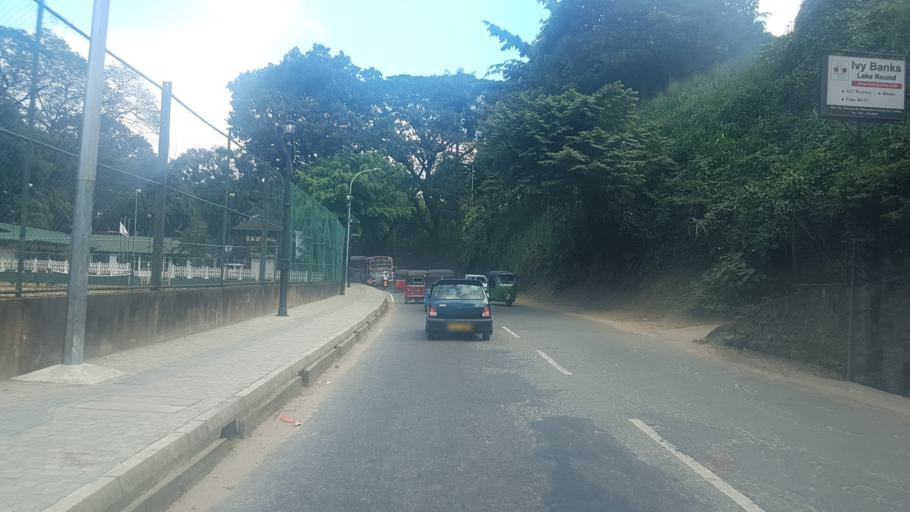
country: LK
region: Central
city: Kandy
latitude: 7.2872
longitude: 80.6465
